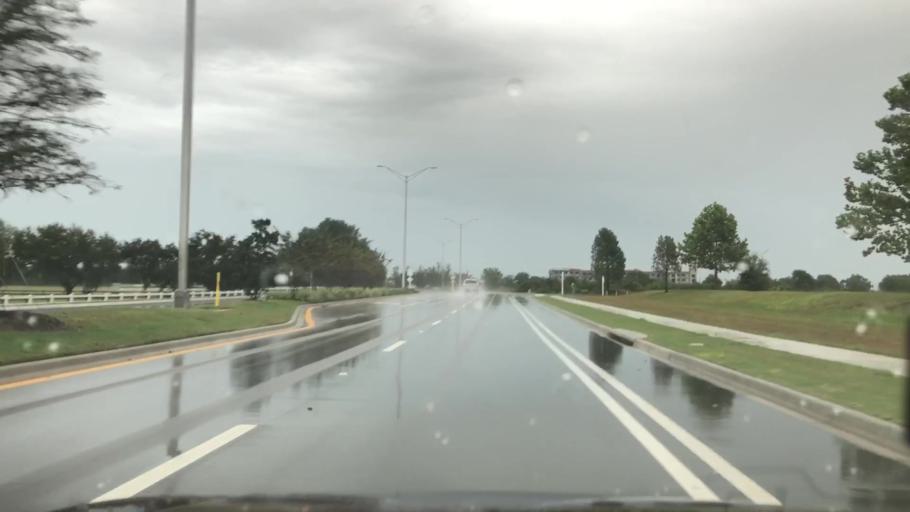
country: US
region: Florida
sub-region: Sarasota County
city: The Meadows
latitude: 27.3796
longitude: -82.3961
